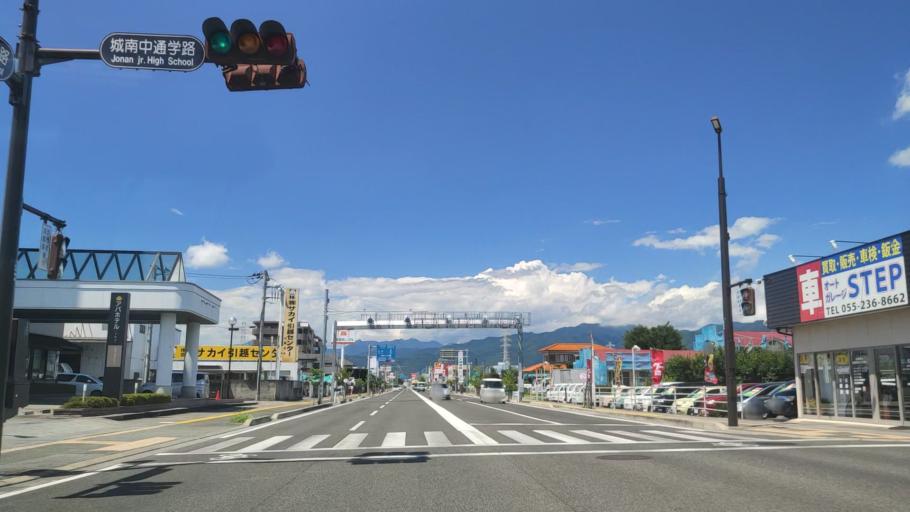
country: JP
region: Yamanashi
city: Kofu-shi
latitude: 35.6222
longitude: 138.5722
